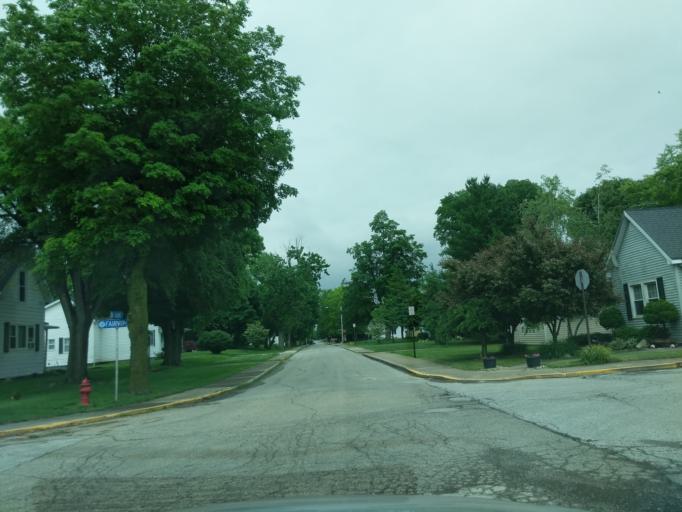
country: US
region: Indiana
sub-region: Tipton County
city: Tipton
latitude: 40.2795
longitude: -86.0459
